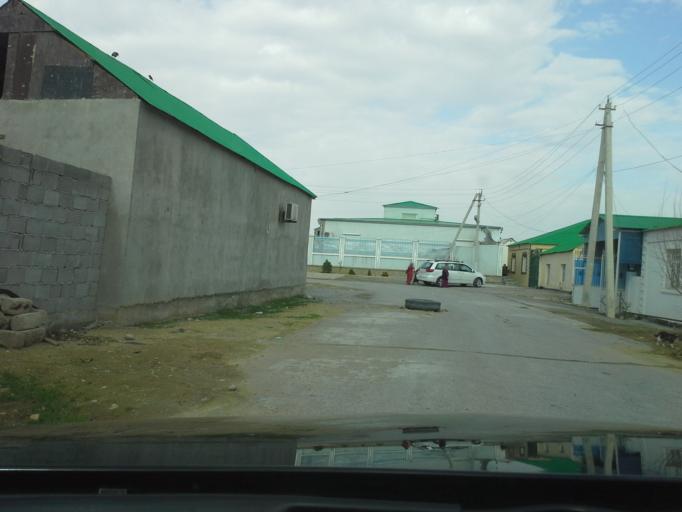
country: TM
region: Ahal
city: Ashgabat
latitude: 37.9897
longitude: 58.2907
